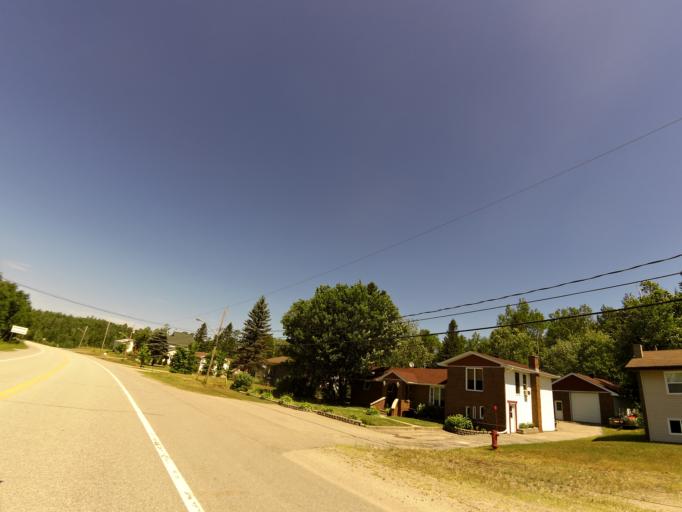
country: CA
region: Quebec
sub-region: Abitibi-Temiscamingue
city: Temiscaming
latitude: 46.7470
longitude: -79.0714
